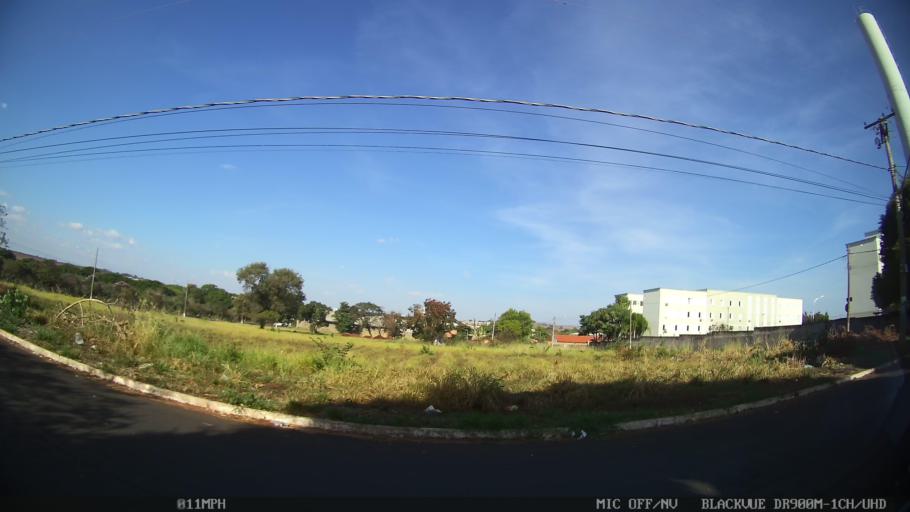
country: BR
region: Sao Paulo
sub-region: Ribeirao Preto
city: Ribeirao Preto
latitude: -21.1790
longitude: -47.7631
